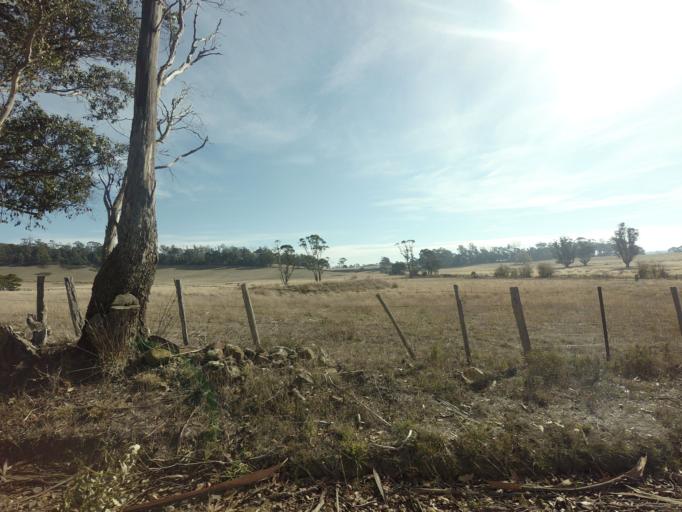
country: AU
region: Tasmania
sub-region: Sorell
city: Sorell
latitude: -42.4796
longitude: 147.4807
